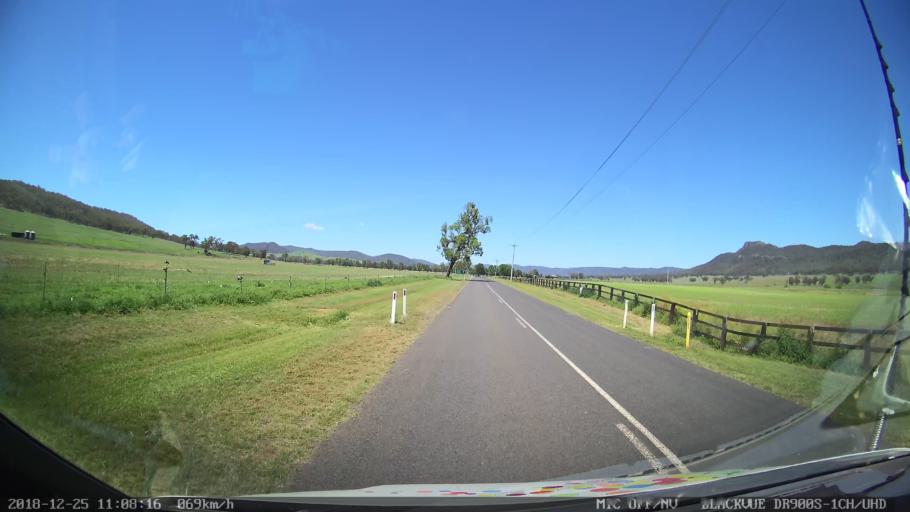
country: AU
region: New South Wales
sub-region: Upper Hunter Shire
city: Merriwa
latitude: -32.4009
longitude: 150.1260
